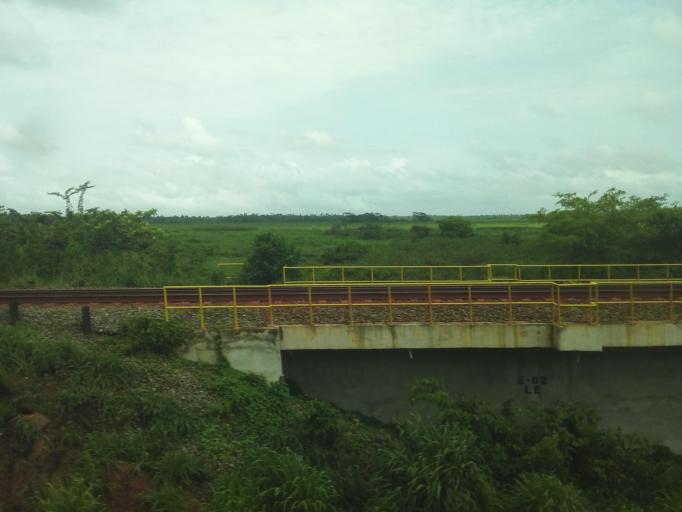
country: BR
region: Maranhao
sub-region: Arari
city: Arari
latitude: -3.5652
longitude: -44.6796
